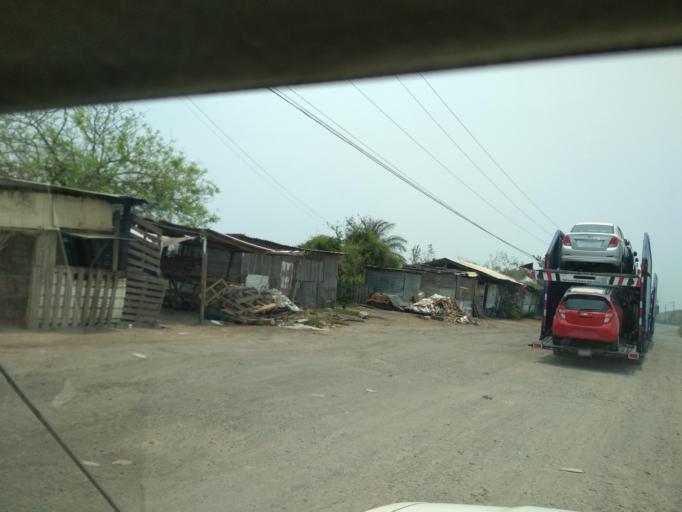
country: MX
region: Veracruz
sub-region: Veracruz
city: Delfino Victoria (Santa Fe)
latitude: 19.2022
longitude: -96.2672
